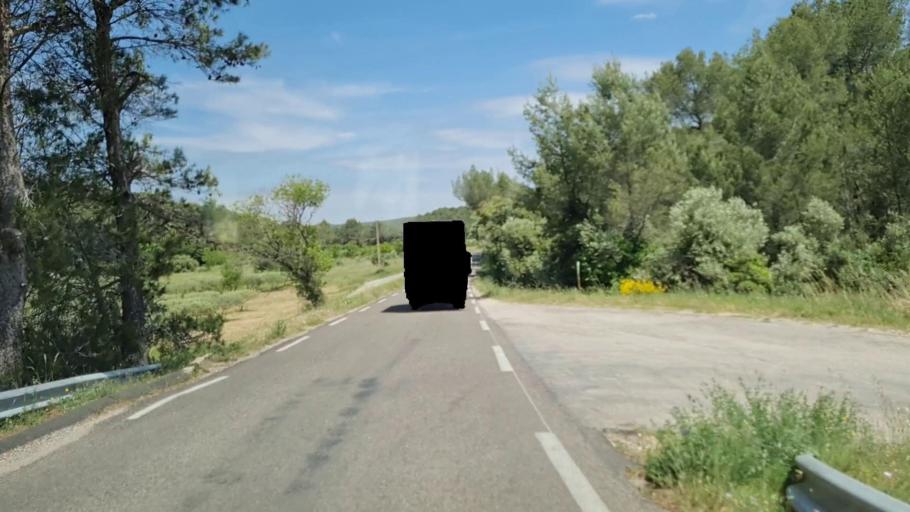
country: FR
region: Languedoc-Roussillon
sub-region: Departement du Gard
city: Saint-Gervasy
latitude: 43.8814
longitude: 4.4682
